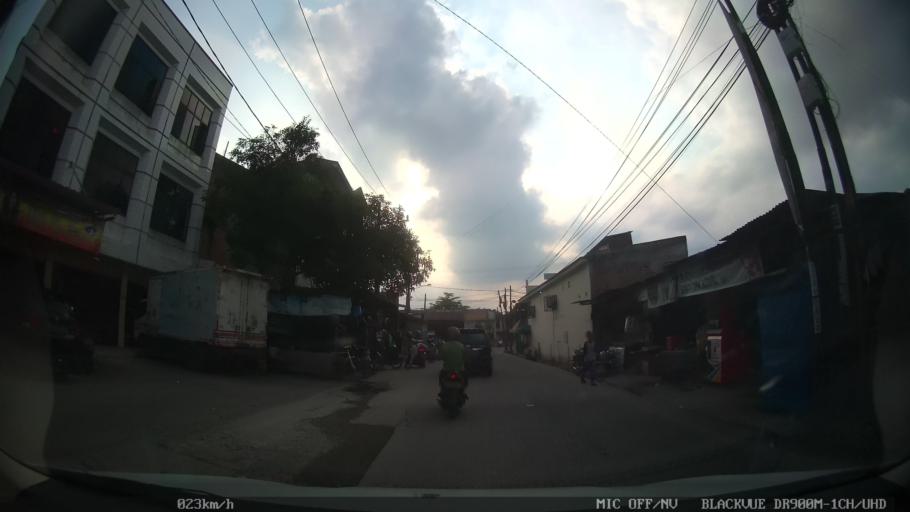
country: ID
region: North Sumatra
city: Medan
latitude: 3.5814
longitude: 98.7302
